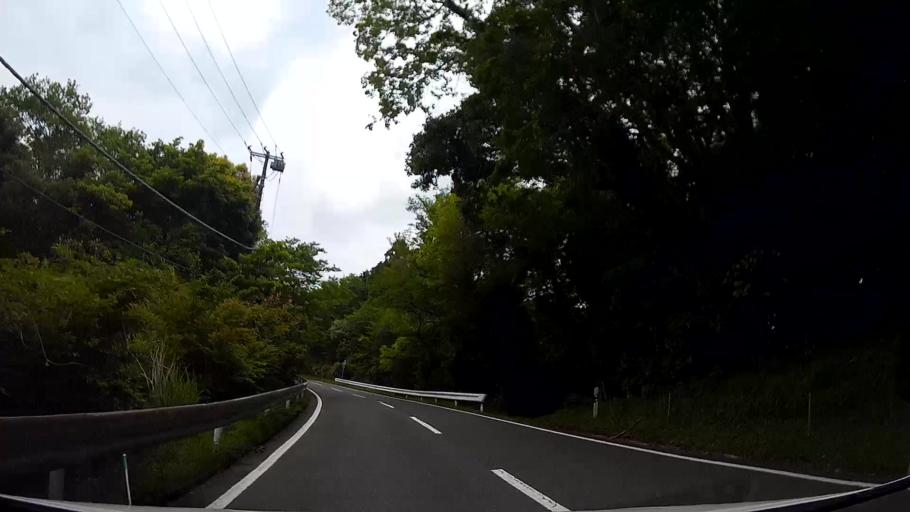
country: JP
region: Shizuoka
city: Ito
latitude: 34.9069
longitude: 139.0787
